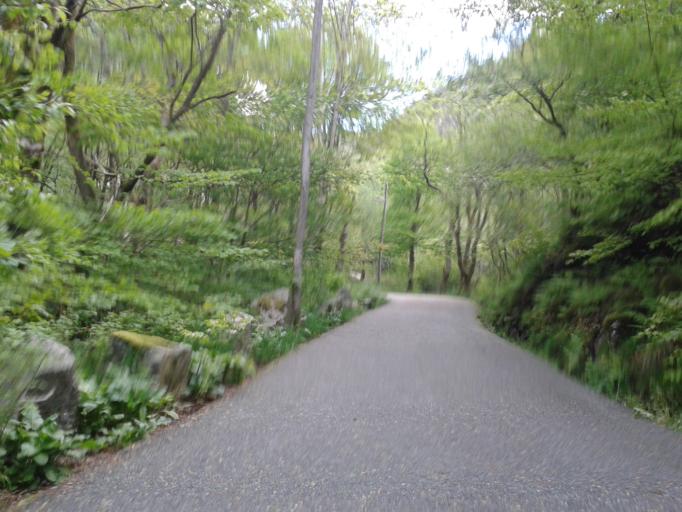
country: NO
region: Hordaland
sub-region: Bergen
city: Bergen
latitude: 60.4187
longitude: 5.3177
